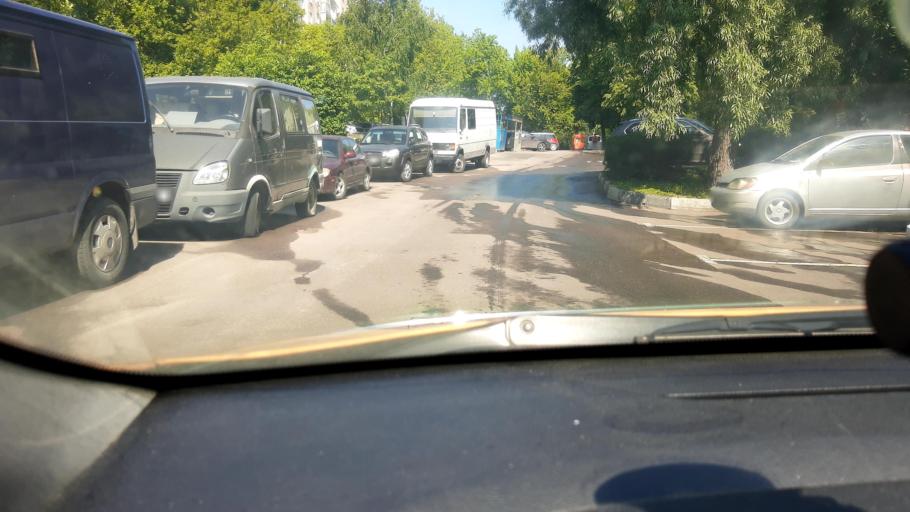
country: RU
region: Moscow
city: Kotlovka
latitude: 55.6796
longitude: 37.6112
